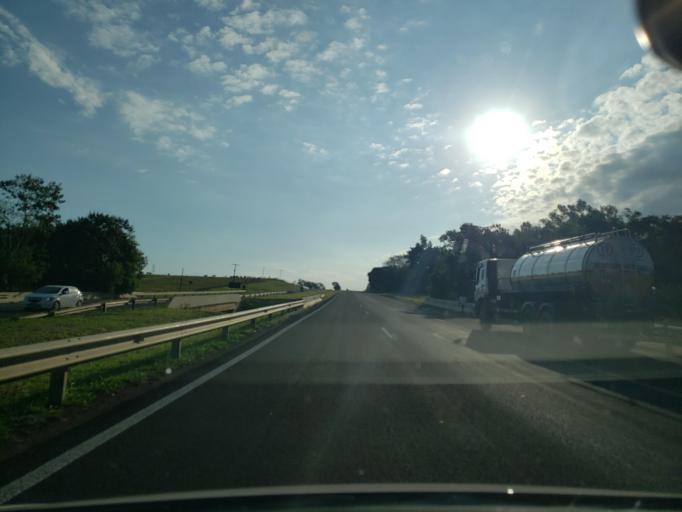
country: BR
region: Sao Paulo
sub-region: Valparaiso
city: Valparaiso
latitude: -21.2094
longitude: -50.8745
